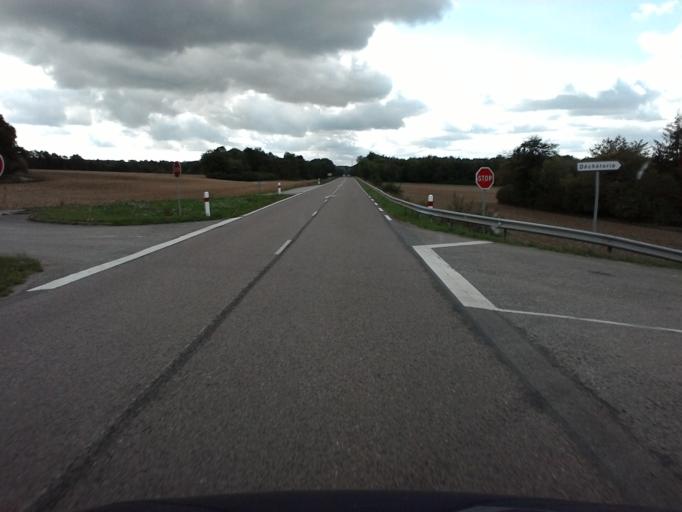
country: FR
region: Lorraine
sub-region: Departement des Vosges
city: Neufchateau
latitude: 48.3803
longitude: 5.7158
